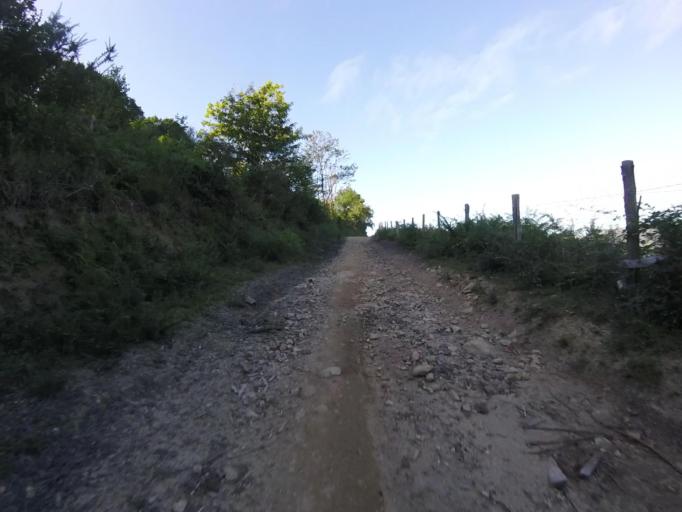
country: ES
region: Basque Country
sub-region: Provincia de Guipuzcoa
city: Irun
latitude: 43.3031
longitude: -1.7473
